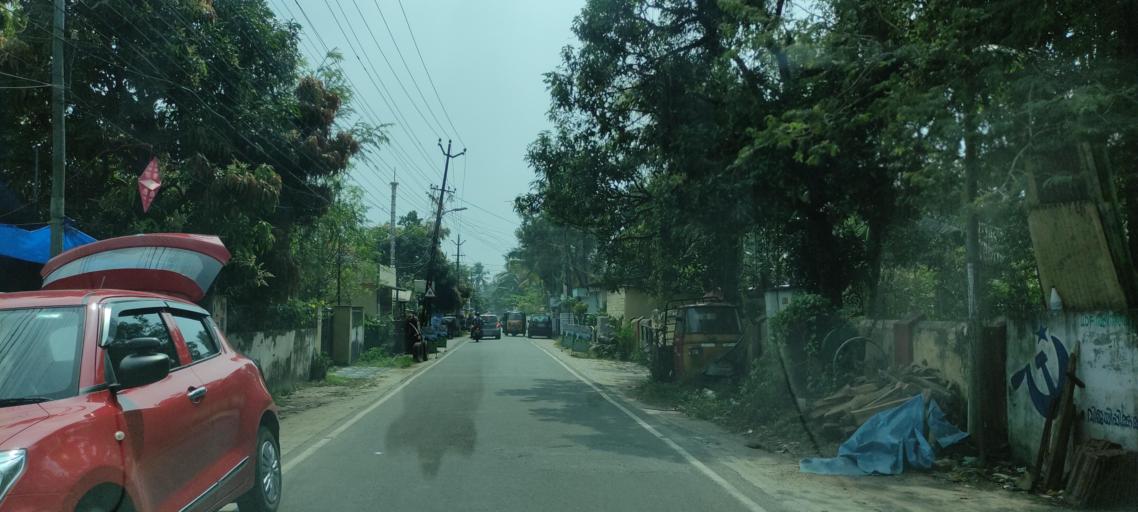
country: IN
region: Kerala
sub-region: Alappuzha
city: Alleppey
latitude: 9.5099
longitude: 76.3345
